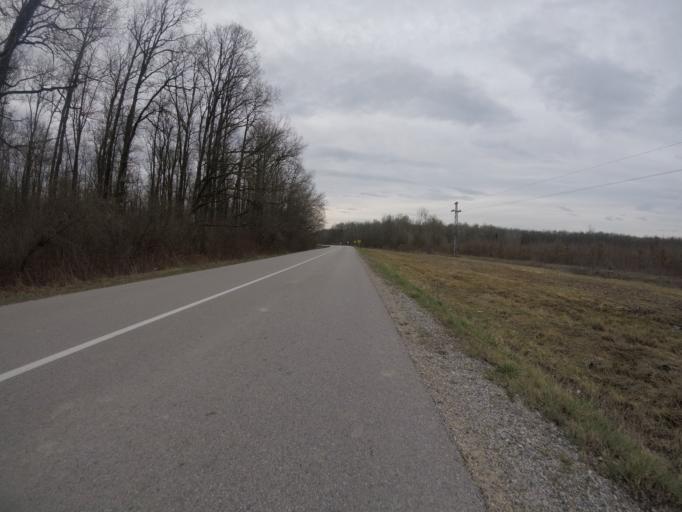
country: HR
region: Zagrebacka
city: Lukavec
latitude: 45.6850
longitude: 15.9799
